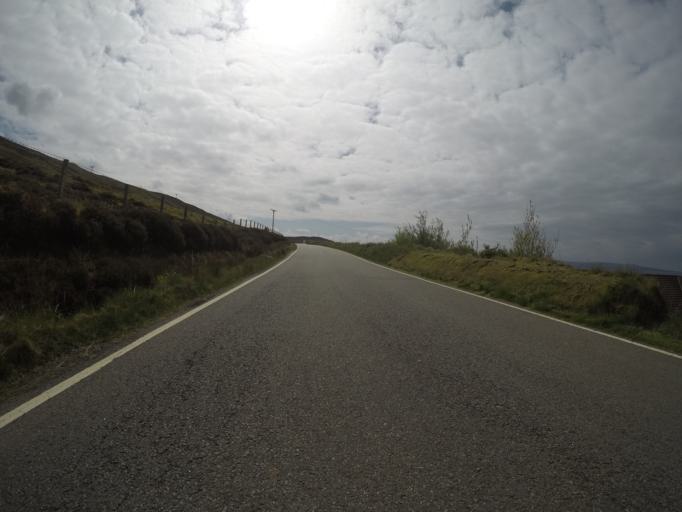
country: GB
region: Scotland
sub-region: Highland
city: Portree
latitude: 57.6110
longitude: -6.3730
